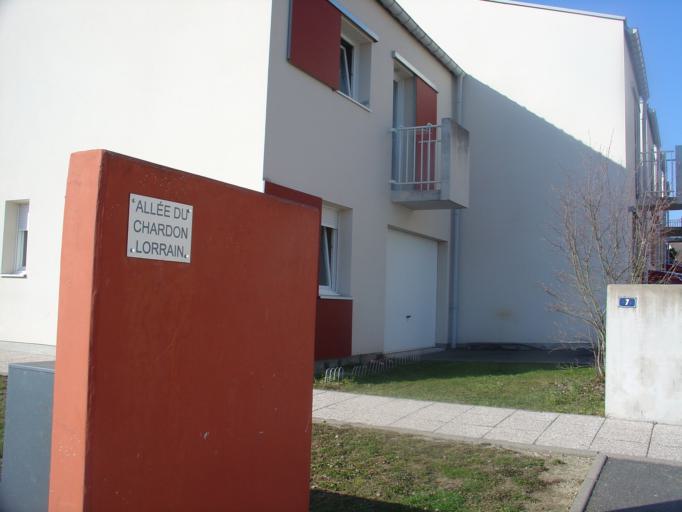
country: FR
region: Lorraine
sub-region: Departement de Meurthe-et-Moselle
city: Toul
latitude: 48.6840
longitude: 5.8724
